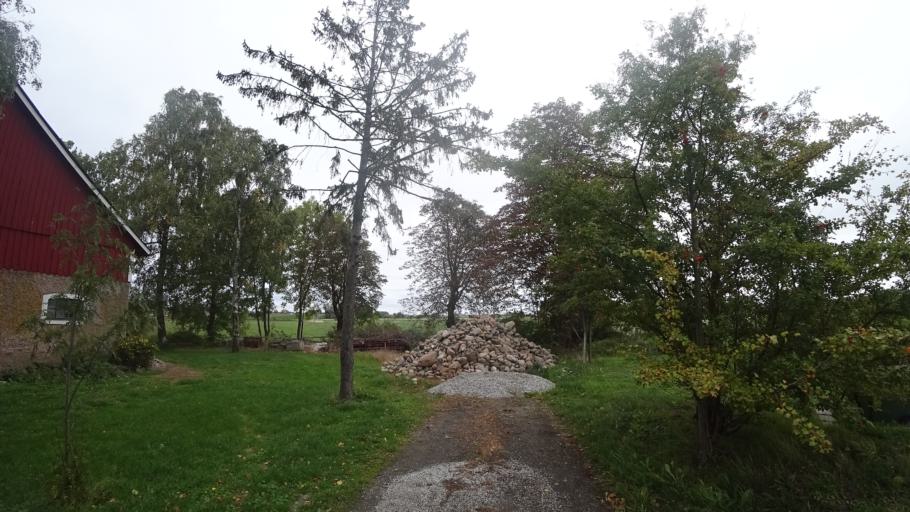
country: SE
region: Skane
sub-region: Kavlinge Kommun
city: Kaevlinge
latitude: 55.7743
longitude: 13.1151
